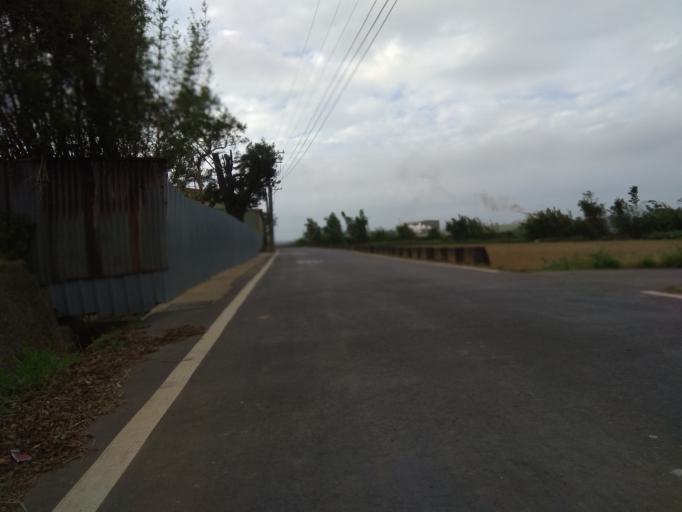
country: TW
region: Taiwan
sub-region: Hsinchu
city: Zhubei
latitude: 24.9740
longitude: 121.0428
